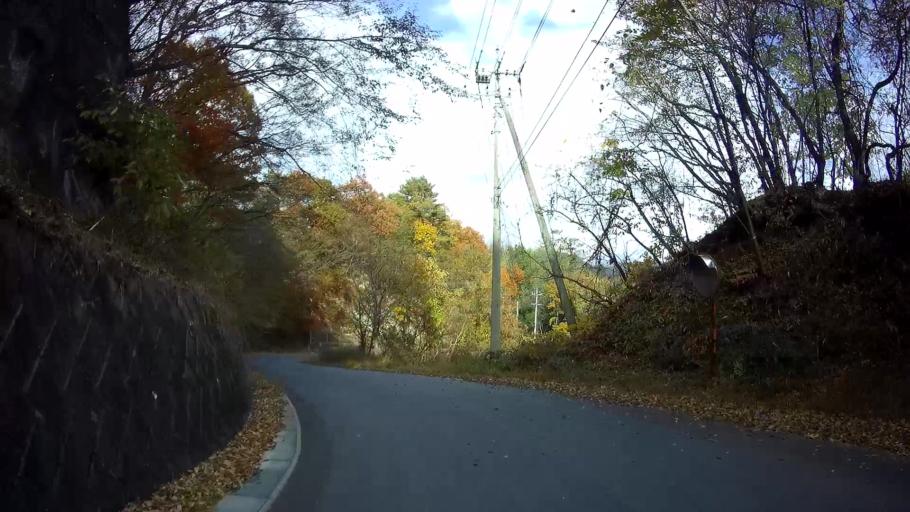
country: JP
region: Gunma
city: Nakanojomachi
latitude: 36.6241
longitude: 138.6314
